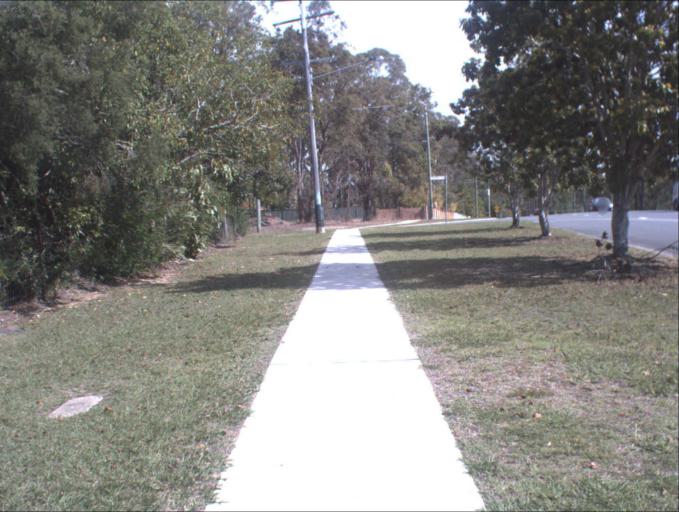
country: AU
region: Queensland
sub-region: Logan
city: Park Ridge South
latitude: -27.7020
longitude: 153.0101
